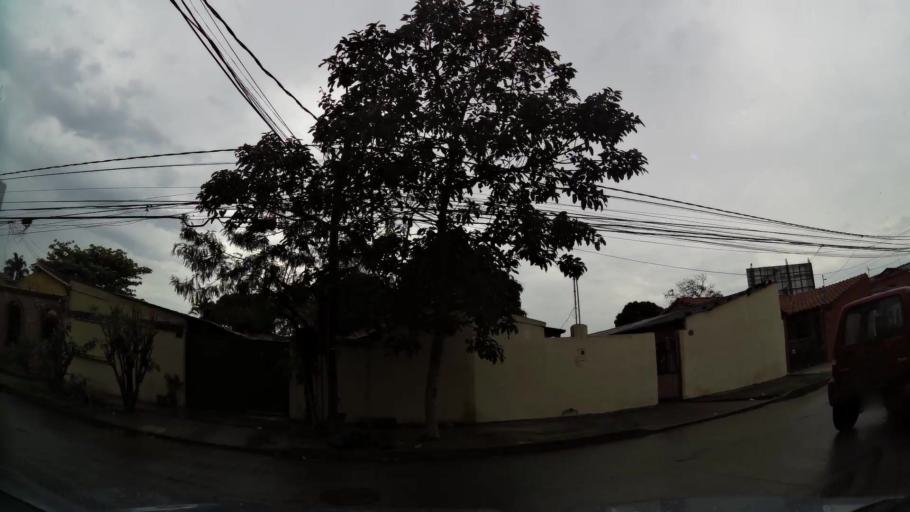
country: BO
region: Santa Cruz
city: Santa Cruz de la Sierra
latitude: -17.7938
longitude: -63.1616
